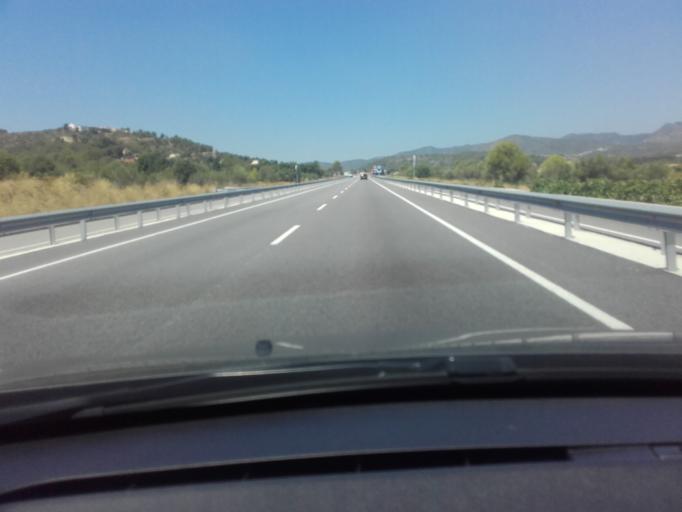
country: ES
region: Catalonia
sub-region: Provincia de Tarragona
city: Albinyana
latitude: 41.2579
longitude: 1.5007
